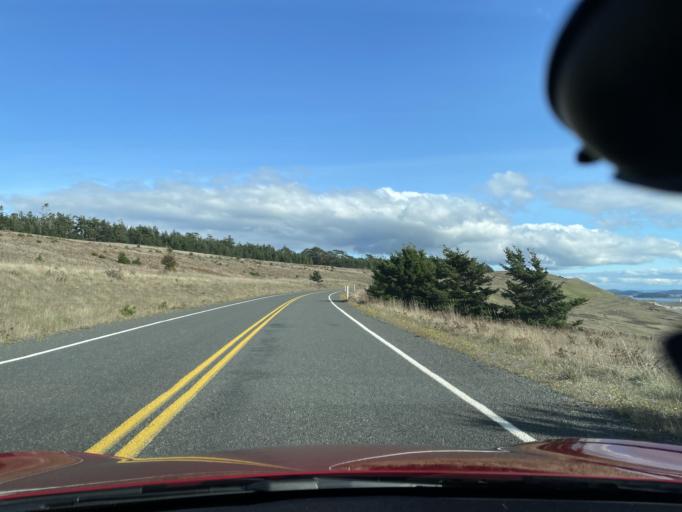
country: US
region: Washington
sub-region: San Juan County
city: Friday Harbor
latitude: 48.4567
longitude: -122.9869
